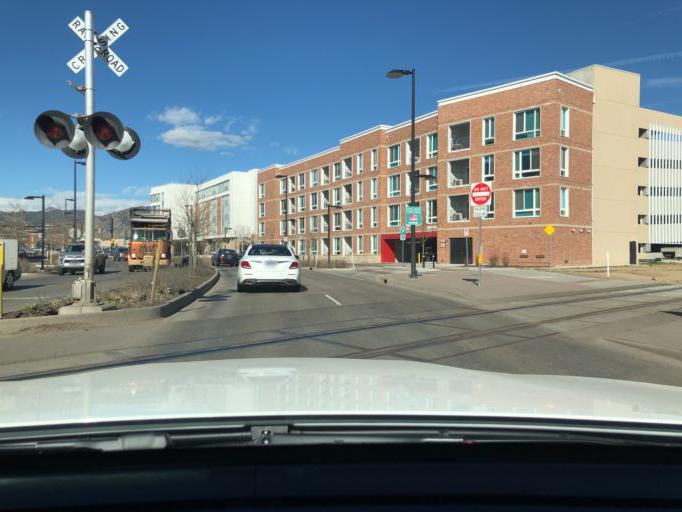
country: US
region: Colorado
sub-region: Boulder County
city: Boulder
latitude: 40.0237
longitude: -105.2501
